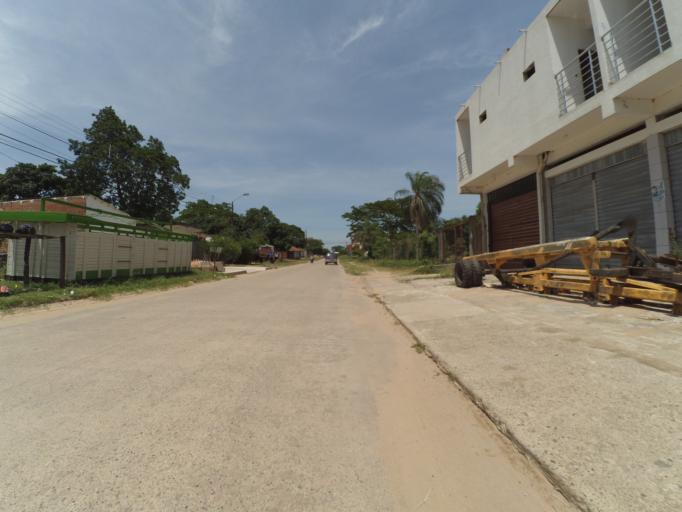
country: BO
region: Santa Cruz
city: Santa Cruz de la Sierra
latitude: -17.8269
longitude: -63.2303
